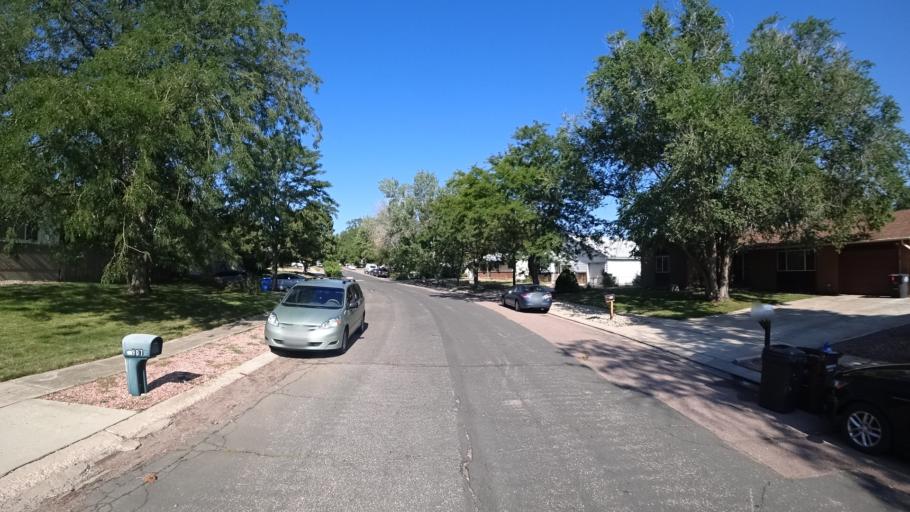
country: US
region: Colorado
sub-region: El Paso County
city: Colorado Springs
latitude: 38.8949
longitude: -104.8377
